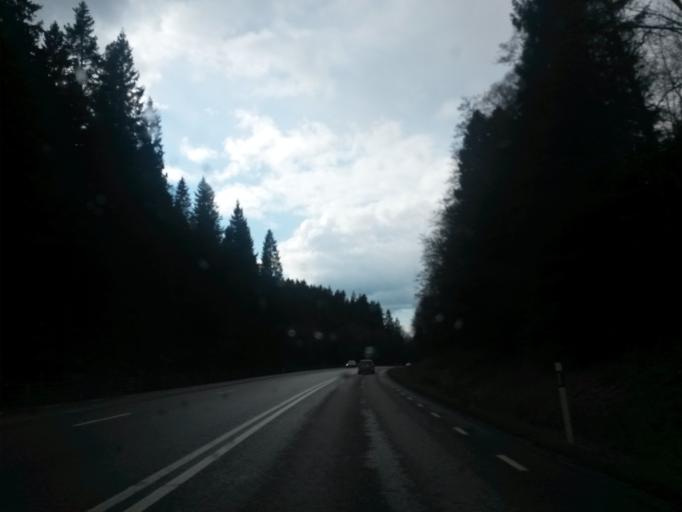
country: SE
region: Vaestra Goetaland
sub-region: Skovde Kommun
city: Skultorp
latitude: 58.3774
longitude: 13.7097
